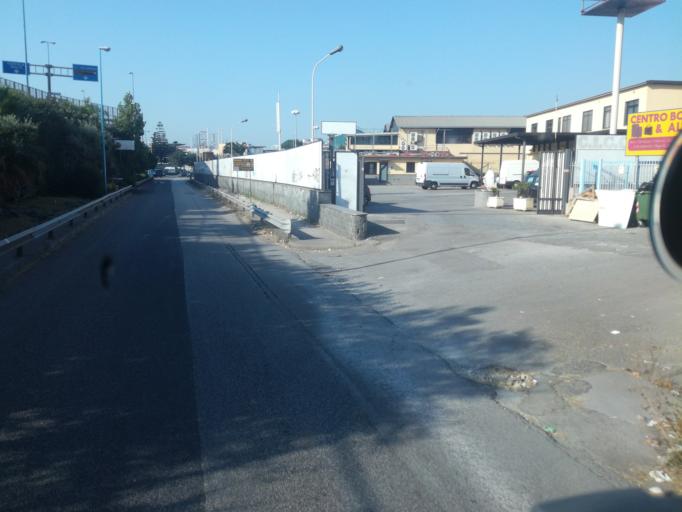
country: IT
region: Campania
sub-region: Provincia di Napoli
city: Arpino
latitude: 40.8929
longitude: 14.3241
